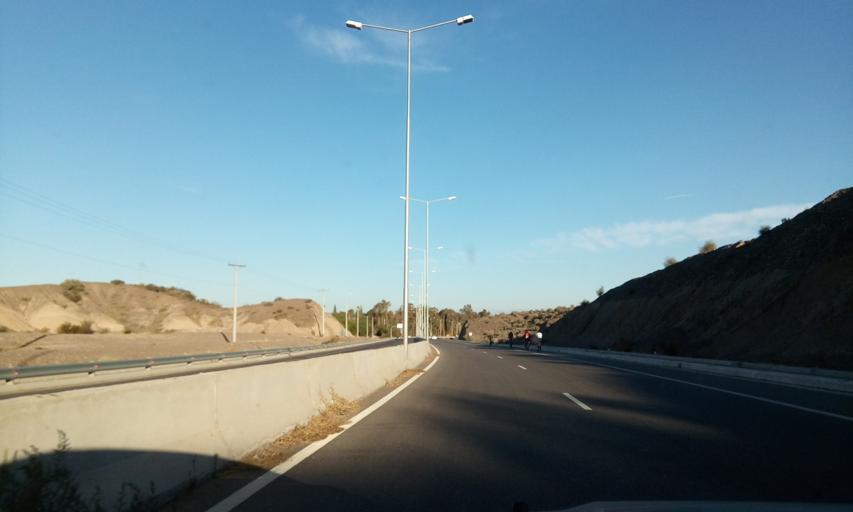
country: AR
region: San Juan
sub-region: Departamento de Rivadavia
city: Rivadavia
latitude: -31.5012
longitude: -68.6482
